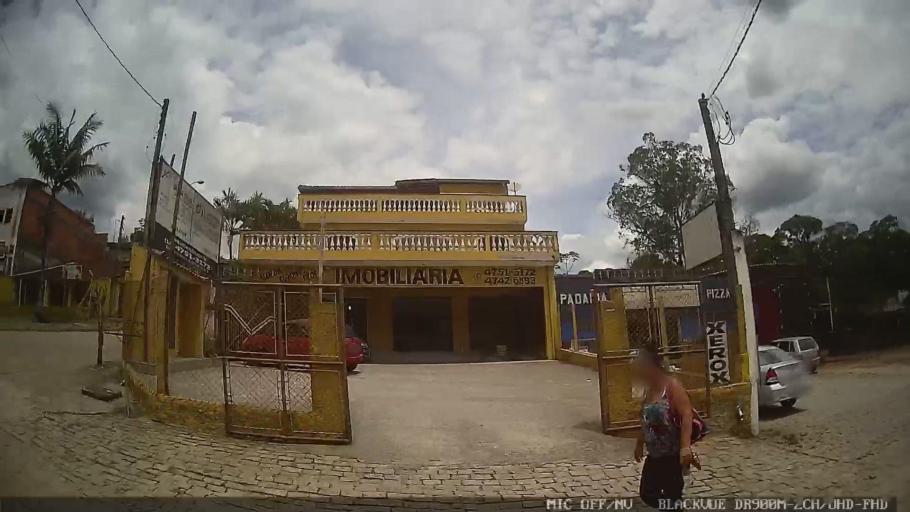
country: BR
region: Sao Paulo
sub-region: Ribeirao Pires
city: Ribeirao Pires
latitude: -23.6689
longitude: -46.3464
